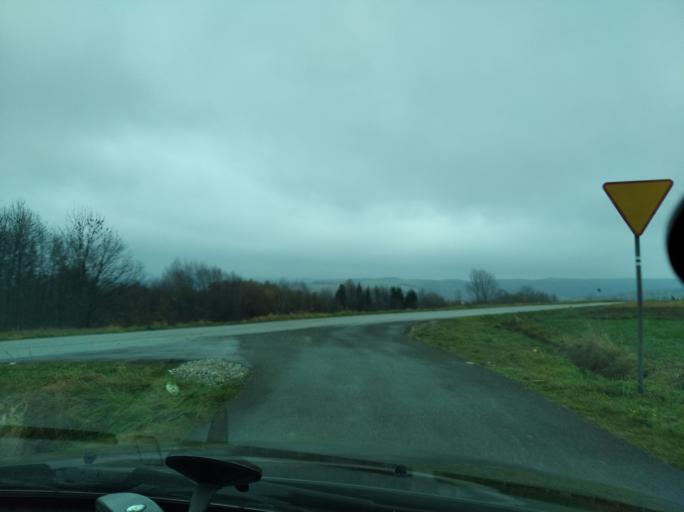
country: PL
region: Subcarpathian Voivodeship
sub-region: Powiat przeworski
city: Jawornik Polski
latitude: 49.8950
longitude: 22.2759
